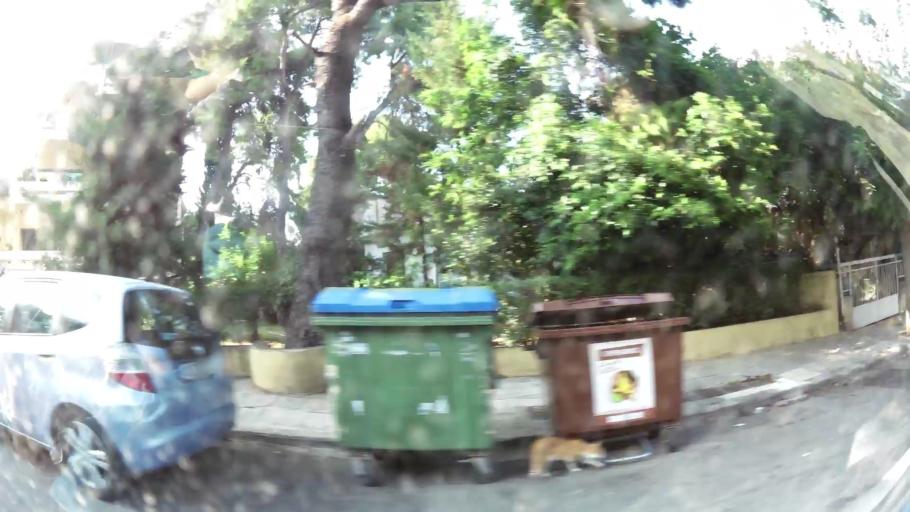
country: GR
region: Attica
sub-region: Nomarchia Athinas
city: Cholargos
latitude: 38.0033
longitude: 23.8173
